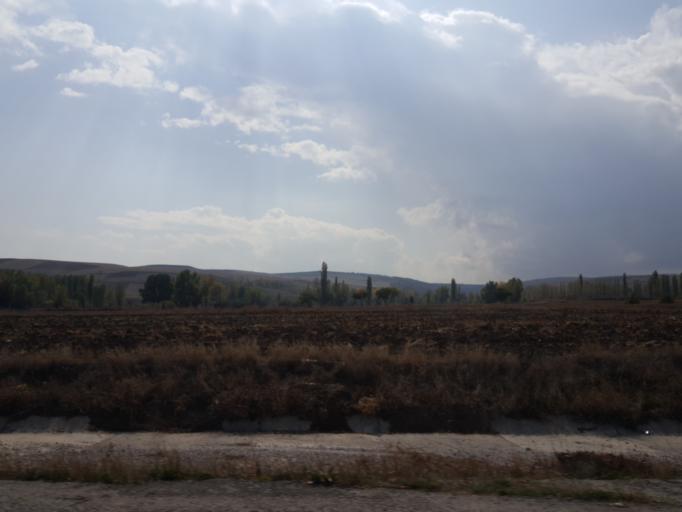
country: TR
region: Corum
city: Alaca
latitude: 40.1390
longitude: 34.8078
